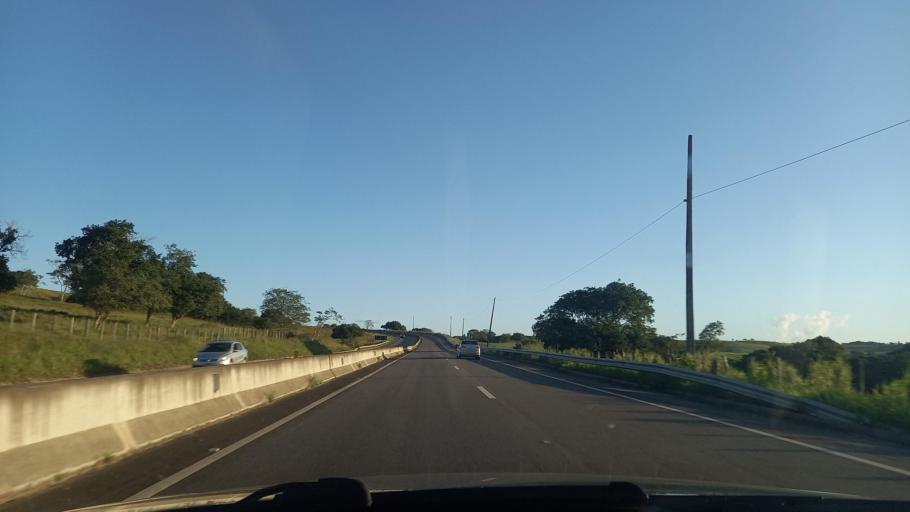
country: BR
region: Alagoas
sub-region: Limoeiro De Anadia
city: Limoeiro de Anadia
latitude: -9.7472
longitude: -36.5022
